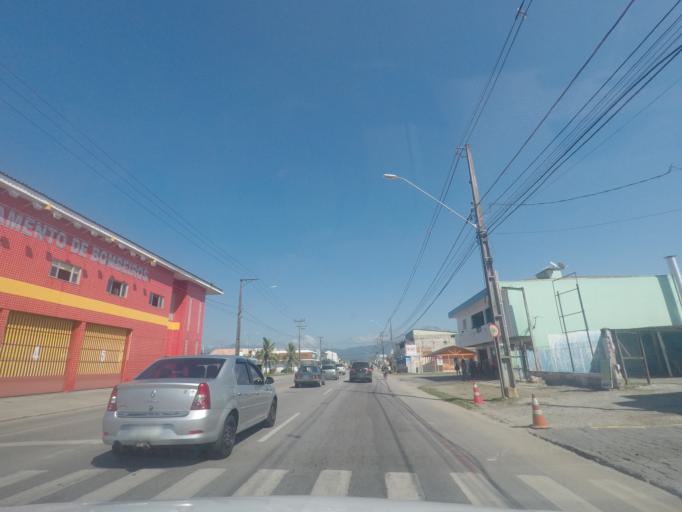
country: BR
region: Parana
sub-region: Paranagua
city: Paranagua
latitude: -25.5631
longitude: -48.5649
